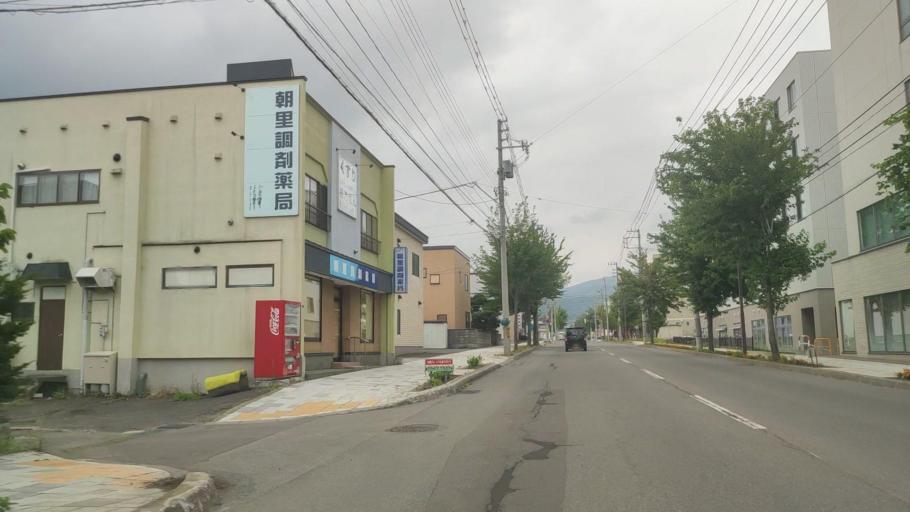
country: JP
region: Hokkaido
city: Otaru
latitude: 43.1733
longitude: 141.0555
